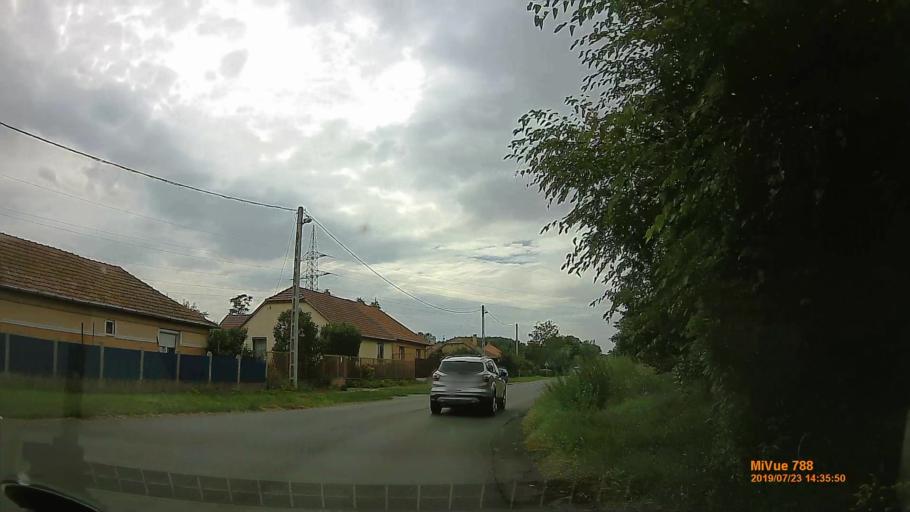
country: HU
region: Szabolcs-Szatmar-Bereg
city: Nyiregyhaza
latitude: 47.9320
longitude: 21.7082
